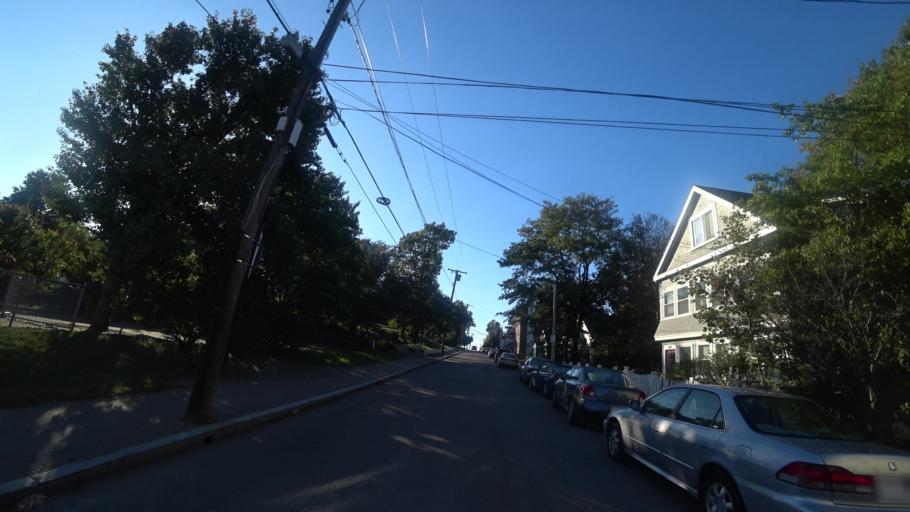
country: US
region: Massachusetts
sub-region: Norfolk County
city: Brookline
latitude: 42.3290
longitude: -71.1029
